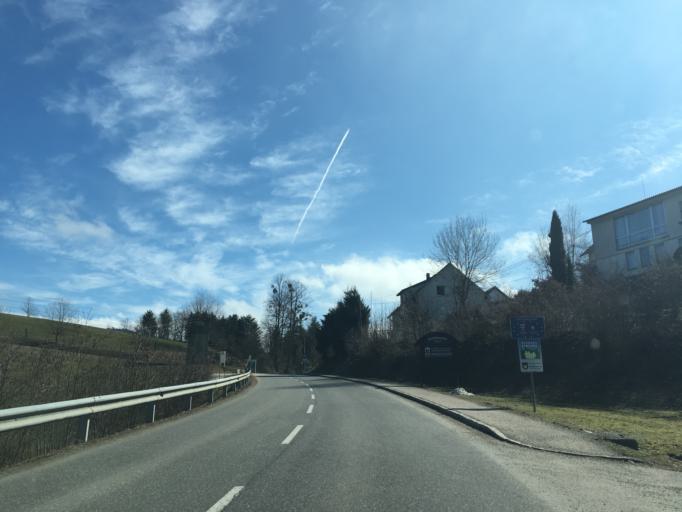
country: AT
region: Lower Austria
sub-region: Politischer Bezirk Melk
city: Dorfstetten
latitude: 48.2769
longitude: 14.9426
